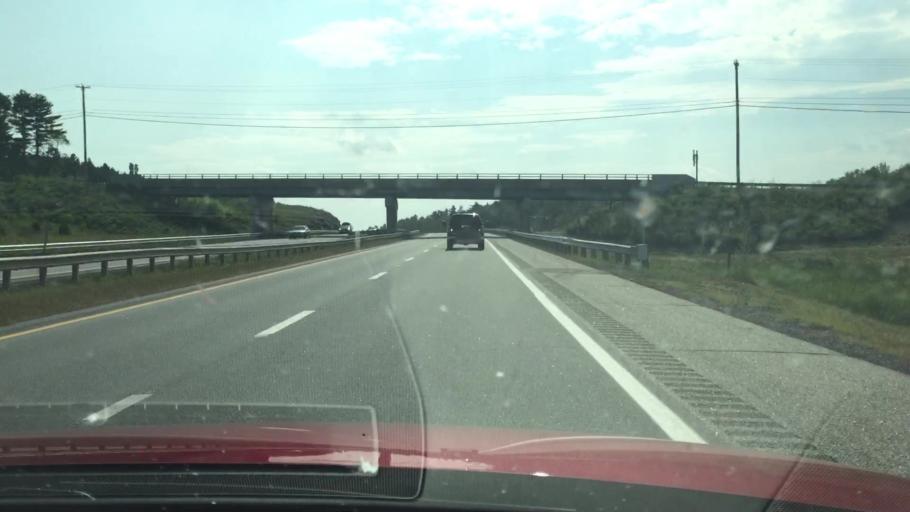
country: US
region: Maine
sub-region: Androscoggin County
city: Sabattus
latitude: 44.1018
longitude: -70.0849
